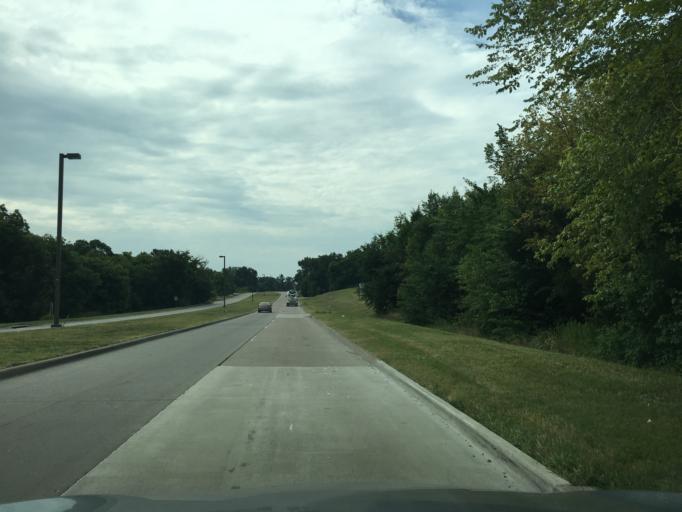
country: US
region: Texas
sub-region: Collin County
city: McKinney
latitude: 33.1981
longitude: -96.5990
